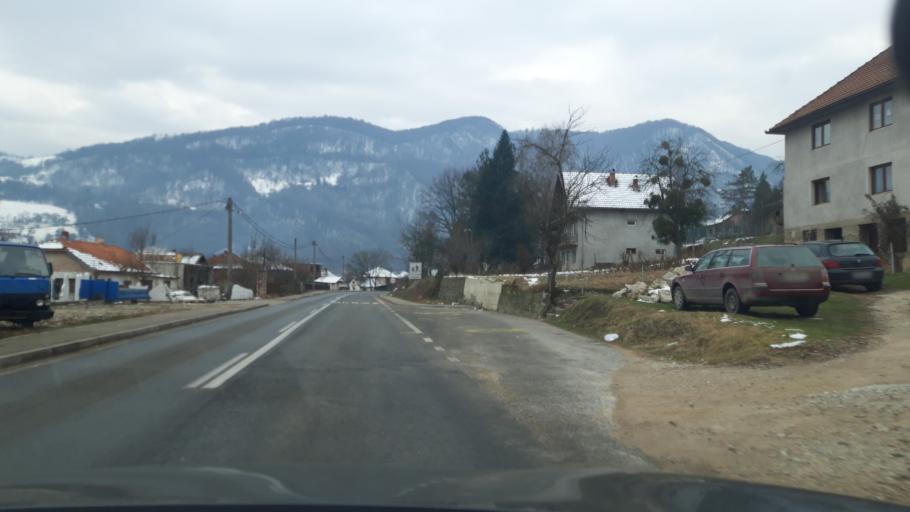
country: RS
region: Central Serbia
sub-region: Macvanski Okrug
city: Mali Zvornik
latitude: 44.2893
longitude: 19.1492
